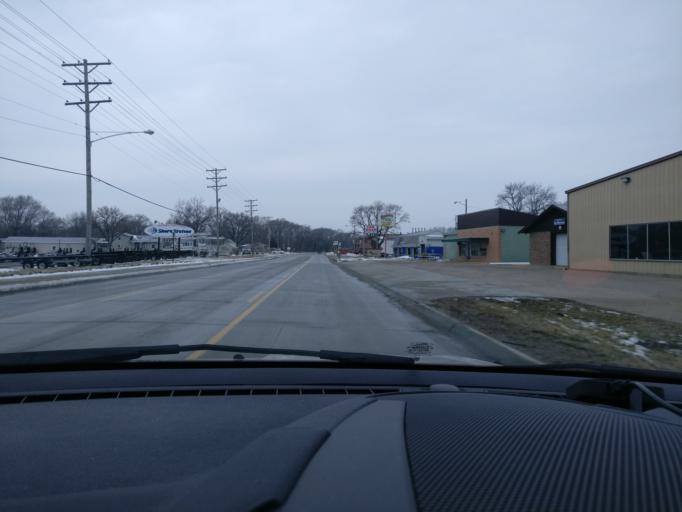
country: US
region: Nebraska
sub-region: Dodge County
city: Fremont
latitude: 41.4369
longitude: -96.5150
